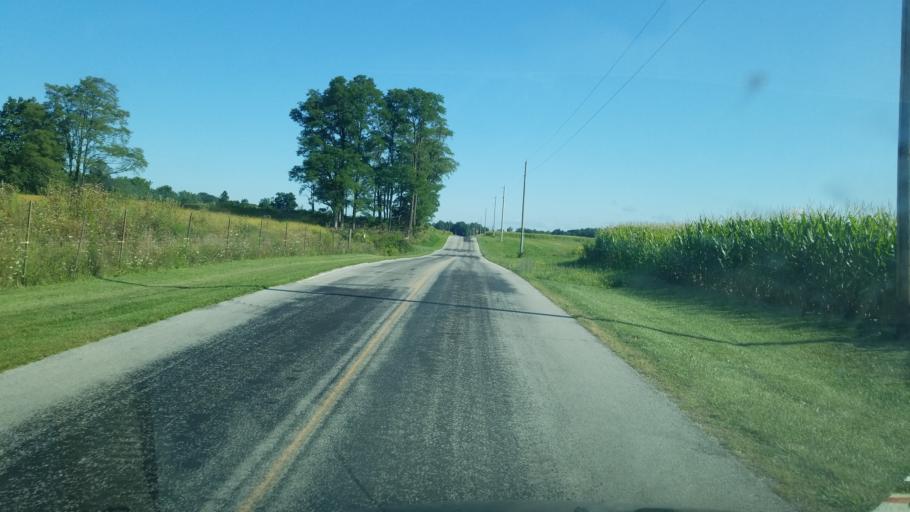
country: US
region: Ohio
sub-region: Wyandot County
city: Carey
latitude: 40.9370
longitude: -83.2997
